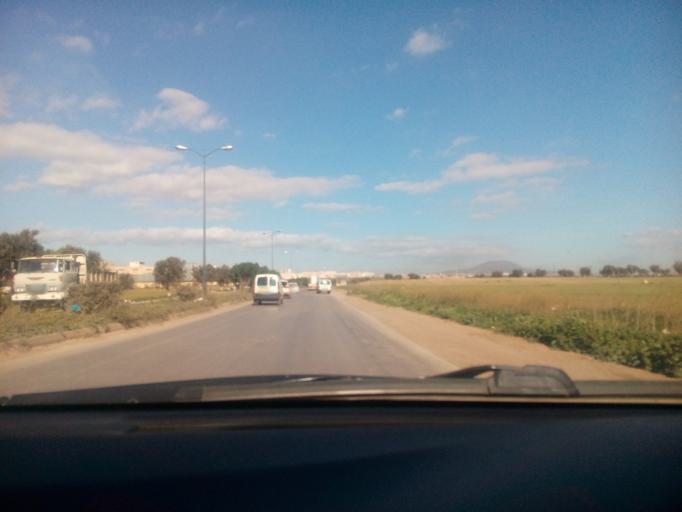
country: DZ
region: Oran
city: Sidi ech Chahmi
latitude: 35.6675
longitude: -0.5666
